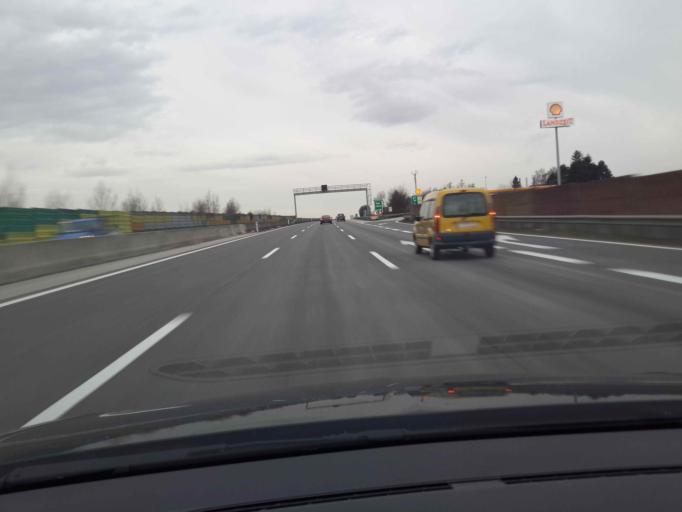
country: AT
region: Lower Austria
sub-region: Politischer Bezirk Amstetten
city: Strengberg
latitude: 48.1133
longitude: 14.6701
